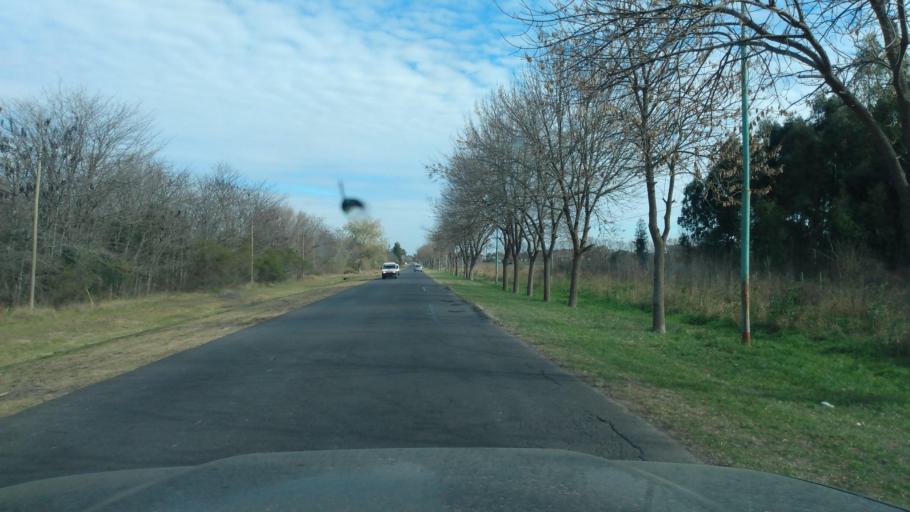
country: AR
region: Buenos Aires
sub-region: Partido de Lujan
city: Lujan
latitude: -34.5749
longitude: -59.1621
